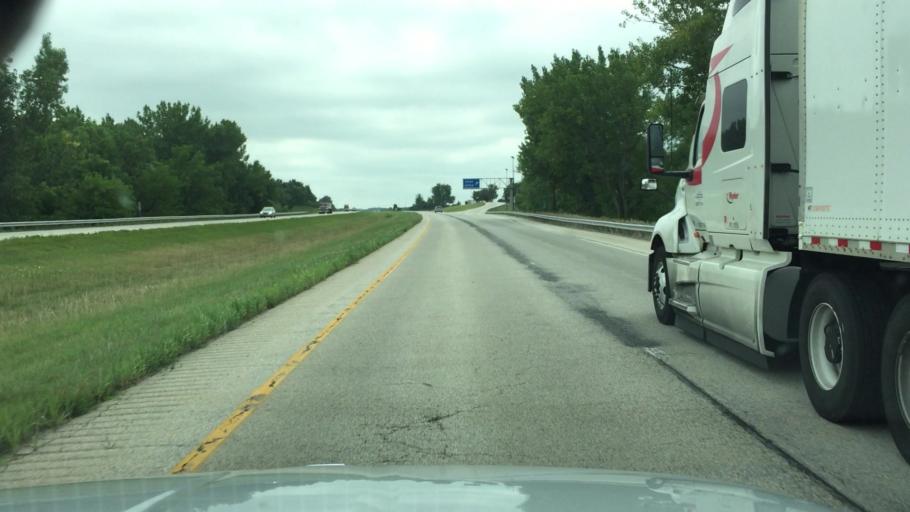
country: US
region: Illinois
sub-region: Henry County
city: Orion
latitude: 41.2385
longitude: -90.3318
